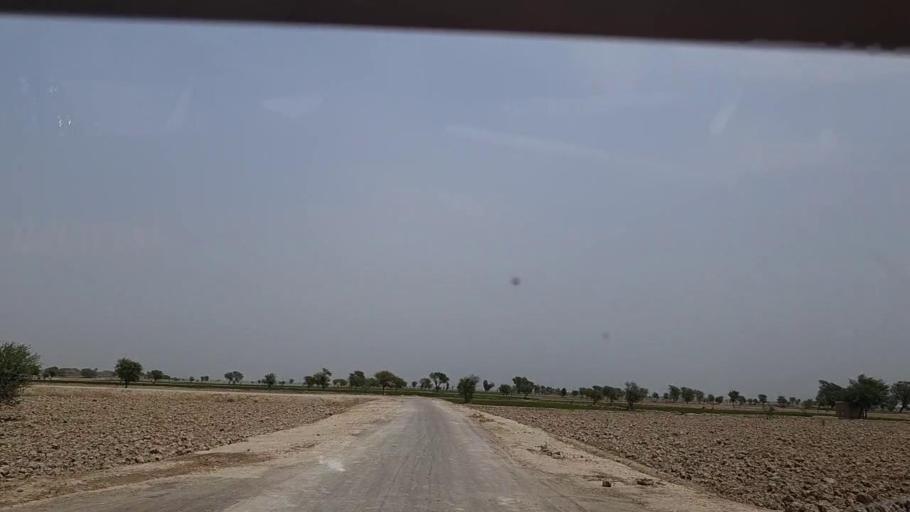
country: PK
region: Sindh
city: Khairpur Nathan Shah
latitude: 27.0171
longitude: 67.6312
